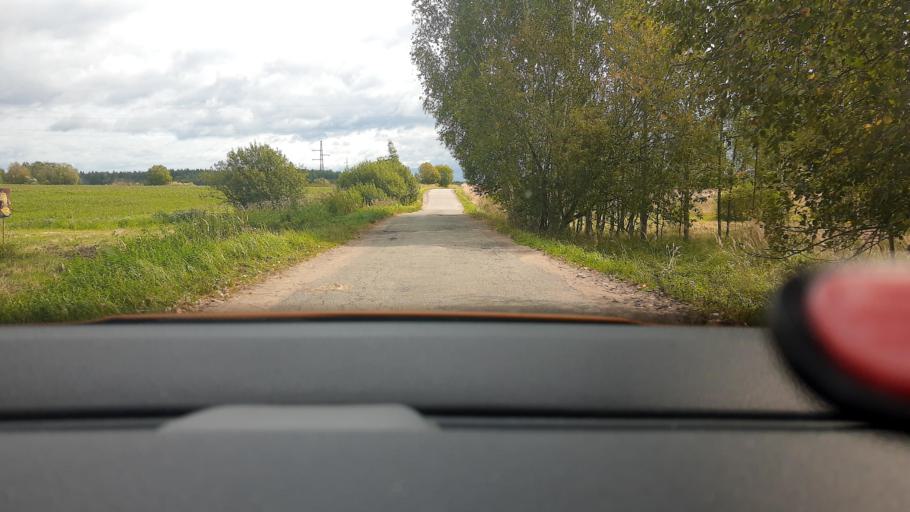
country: RU
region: Moskovskaya
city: Krasnoarmeysk
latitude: 56.0894
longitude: 38.0298
